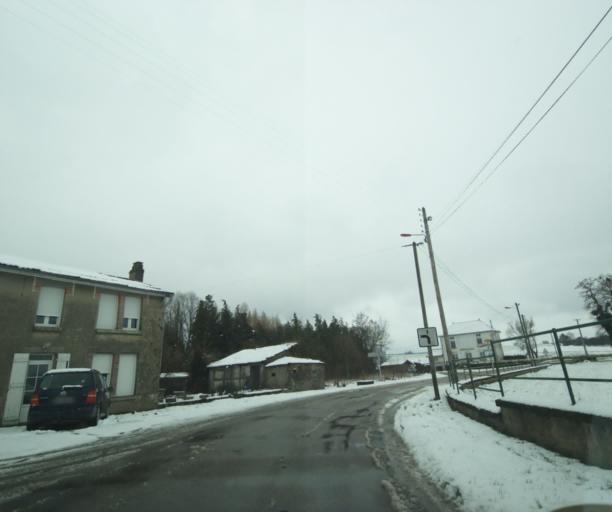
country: FR
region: Champagne-Ardenne
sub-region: Departement de la Haute-Marne
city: Laneuville-a-Remy
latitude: 48.4098
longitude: 4.8457
